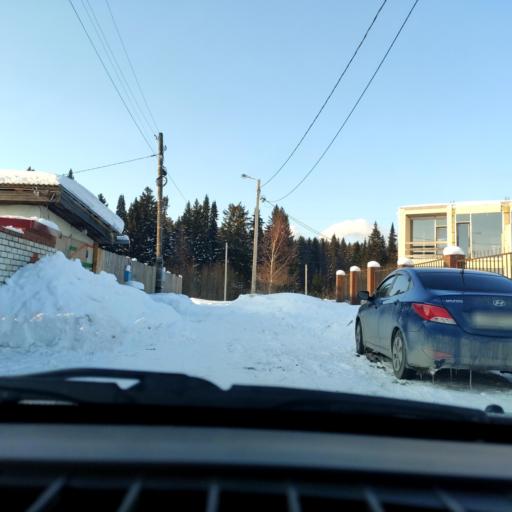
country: RU
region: Perm
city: Froly
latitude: 57.9505
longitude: 56.3050
